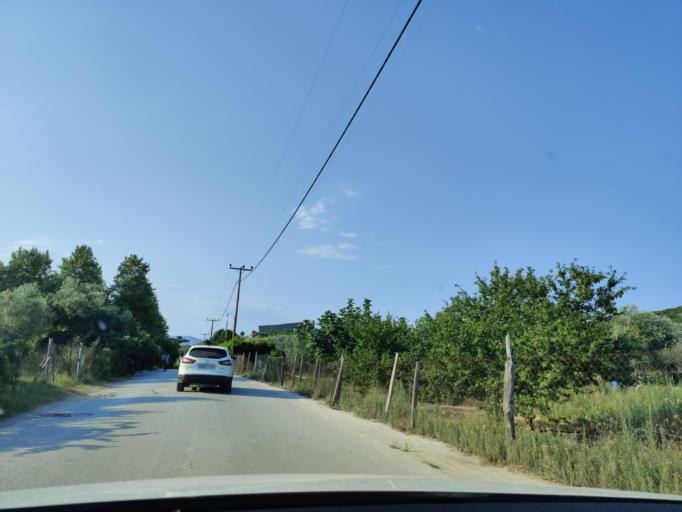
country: GR
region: East Macedonia and Thrace
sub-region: Nomos Kavalas
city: Nea Peramos
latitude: 40.8210
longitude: 24.3078
